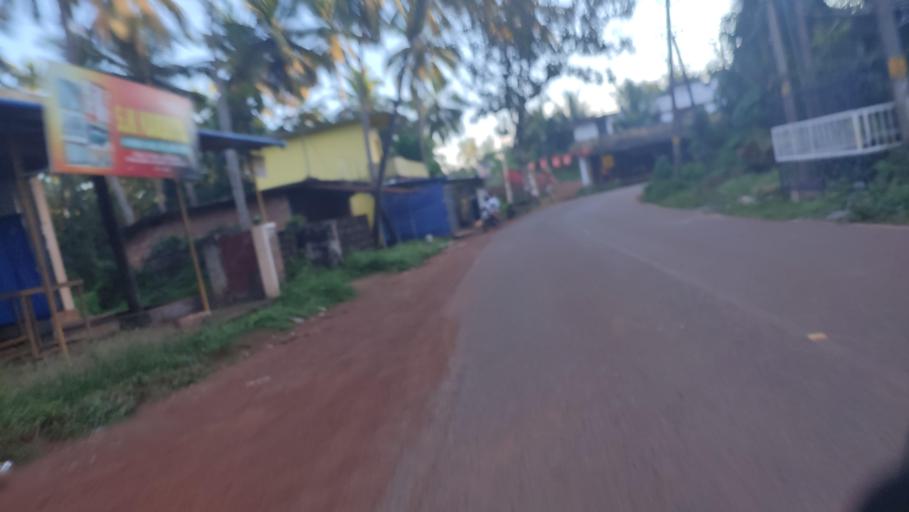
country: IN
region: Kerala
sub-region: Kasaragod District
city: Kannangad
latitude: 12.3998
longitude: 75.0634
